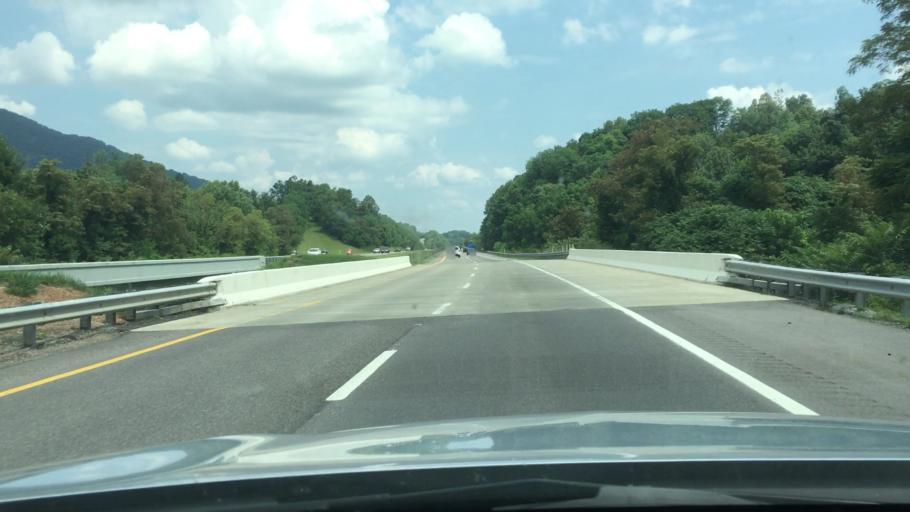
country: US
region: Tennessee
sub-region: Unicoi County
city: Unicoi
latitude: 36.2410
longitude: -82.3271
